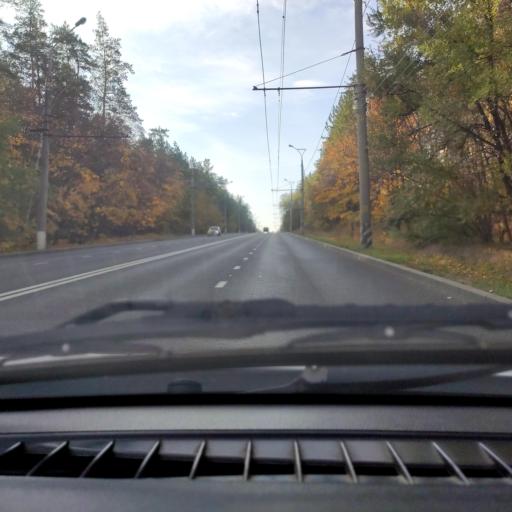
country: RU
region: Samara
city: Zhigulevsk
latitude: 53.4964
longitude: 49.4630
